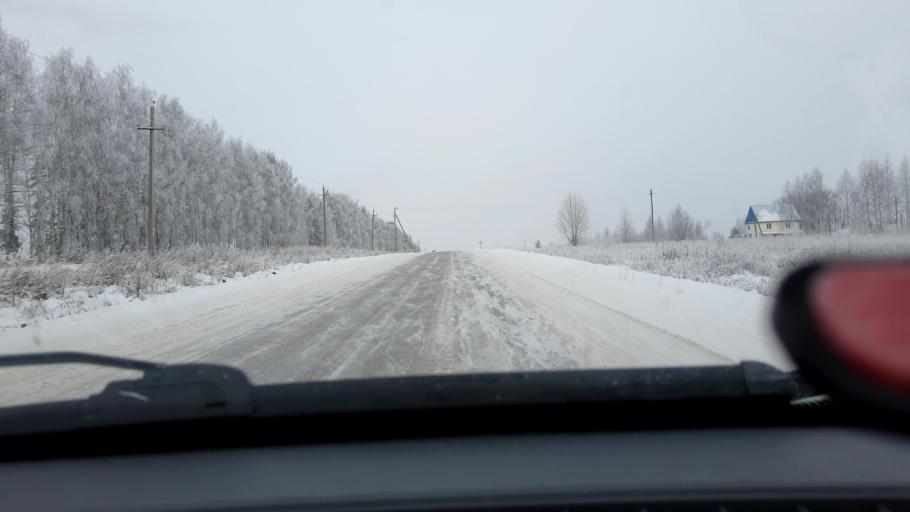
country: RU
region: Bashkortostan
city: Iglino
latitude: 54.6562
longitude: 56.4253
